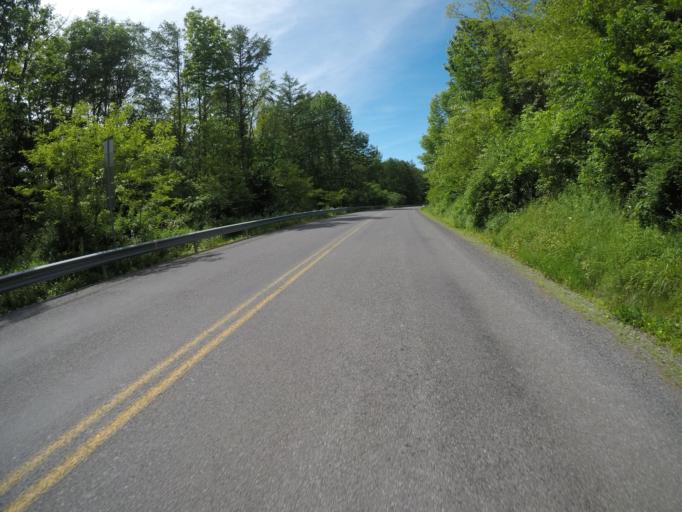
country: US
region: New York
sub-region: Sullivan County
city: Livingston Manor
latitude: 42.0898
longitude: -74.8189
